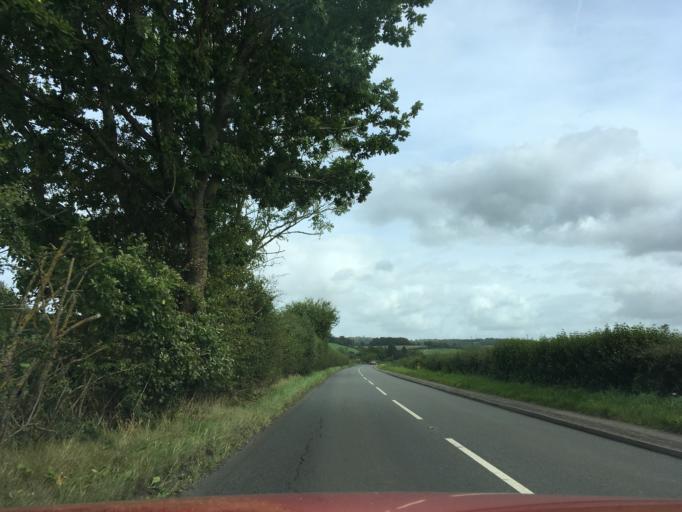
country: GB
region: England
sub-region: Gloucestershire
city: Wotton-under-Edge
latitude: 51.6351
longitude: -2.3724
